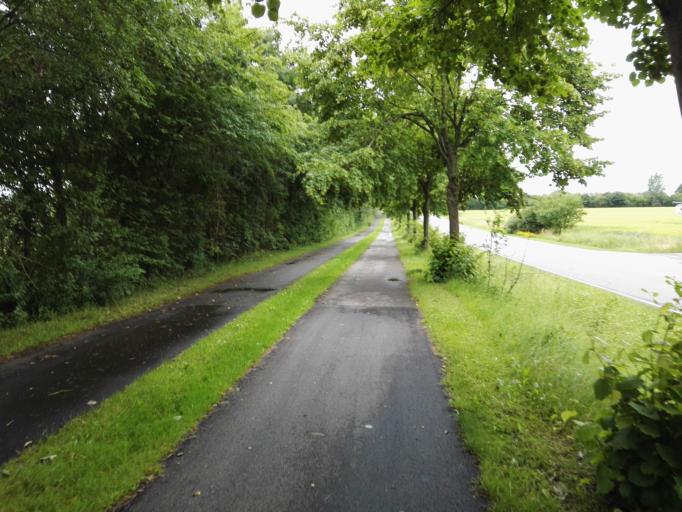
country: DK
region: Capital Region
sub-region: Egedal Kommune
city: Olstykke
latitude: 55.7791
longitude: 12.1584
